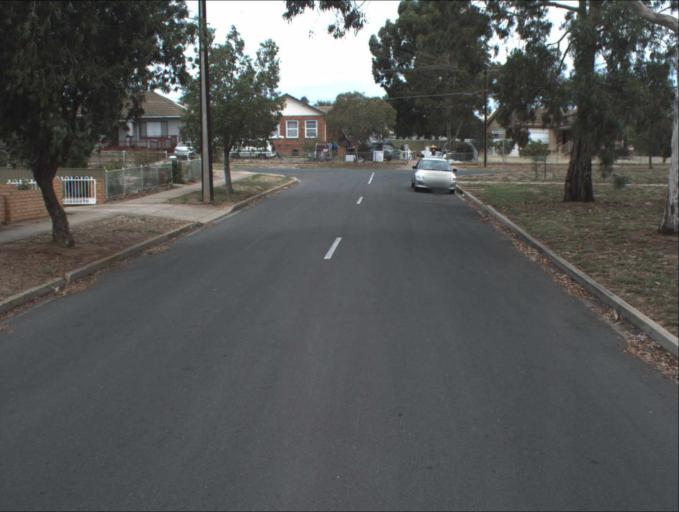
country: AU
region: South Australia
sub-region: Port Adelaide Enfield
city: Enfield
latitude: -34.8526
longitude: 138.6027
